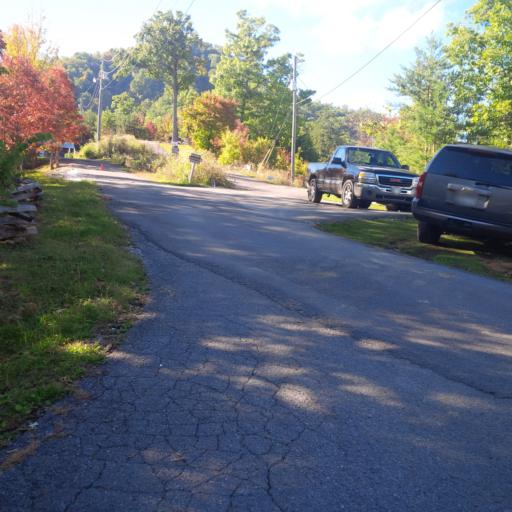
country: US
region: Tennessee
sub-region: Sevier County
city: Pigeon Forge
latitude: 35.6986
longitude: -83.6600
